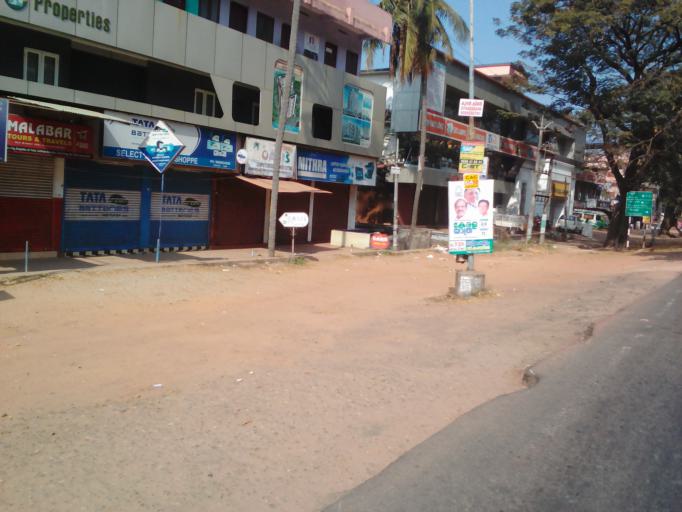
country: IN
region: Kerala
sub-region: Kozhikode
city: Badagara
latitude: 11.5997
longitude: 75.5931
